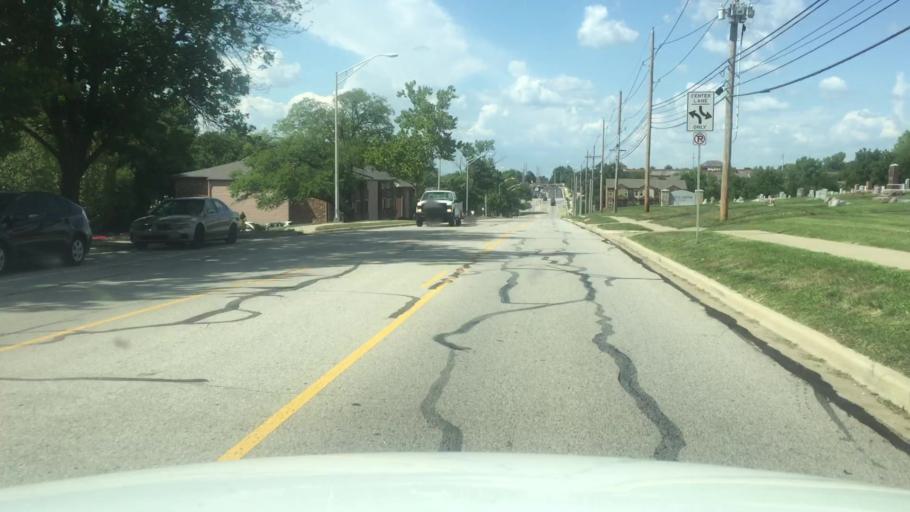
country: US
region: Kansas
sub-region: Johnson County
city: Lenexa
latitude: 38.9671
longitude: -94.7422
